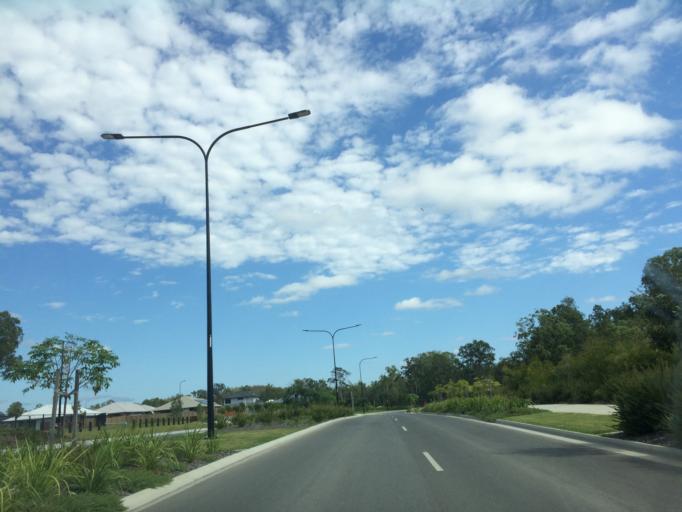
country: AU
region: Queensland
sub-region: Logan
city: North Maclean
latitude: -27.8035
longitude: 152.9460
